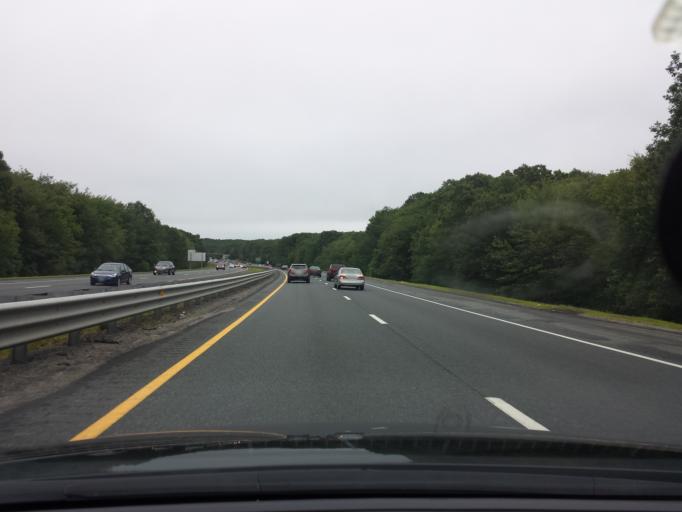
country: US
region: Rhode Island
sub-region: Kent County
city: West Warwick
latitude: 41.6594
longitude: -71.5357
